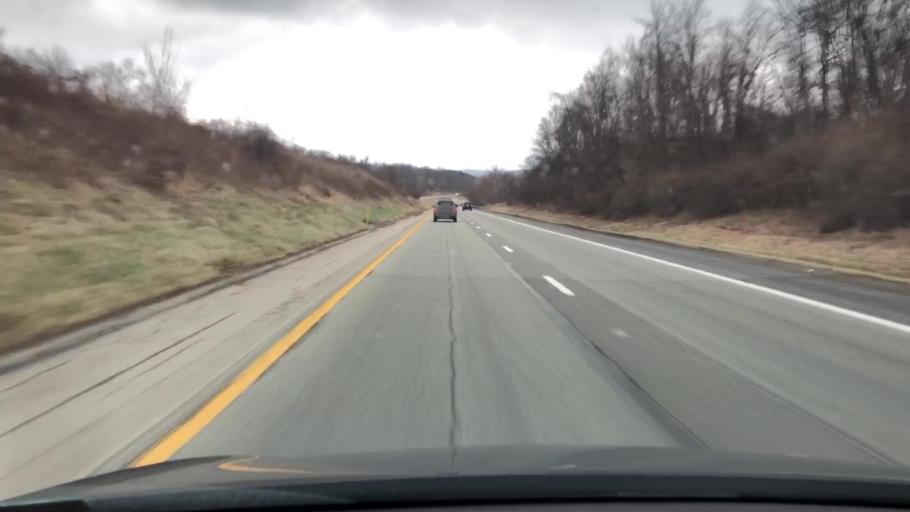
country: US
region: Pennsylvania
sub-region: Washington County
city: East Washington
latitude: 40.0715
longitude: -80.1897
